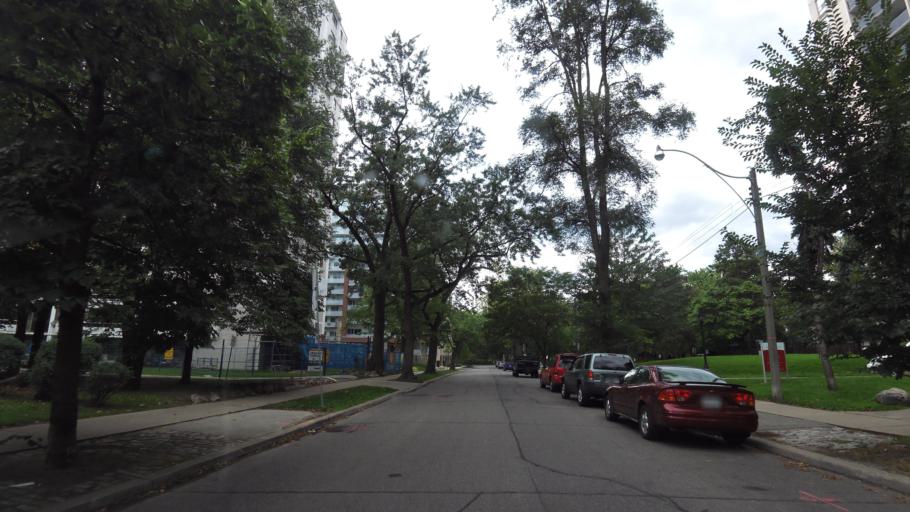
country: CA
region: Ontario
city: Toronto
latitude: 43.6556
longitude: -79.4643
